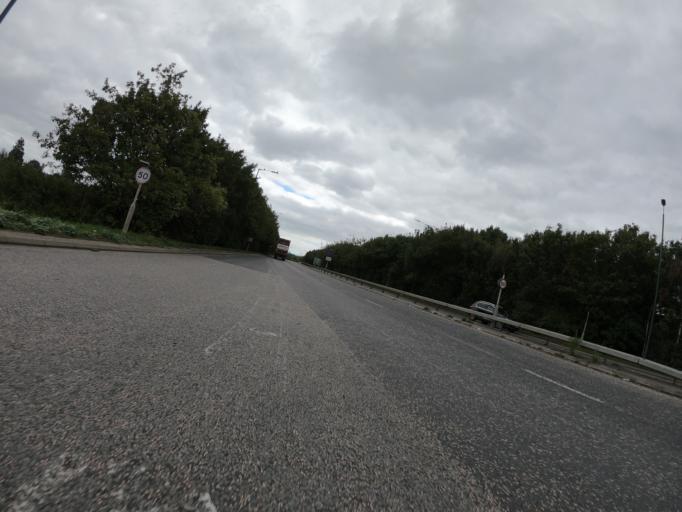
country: GB
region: England
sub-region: Greater London
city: Belvedere
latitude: 51.4970
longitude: 0.1584
